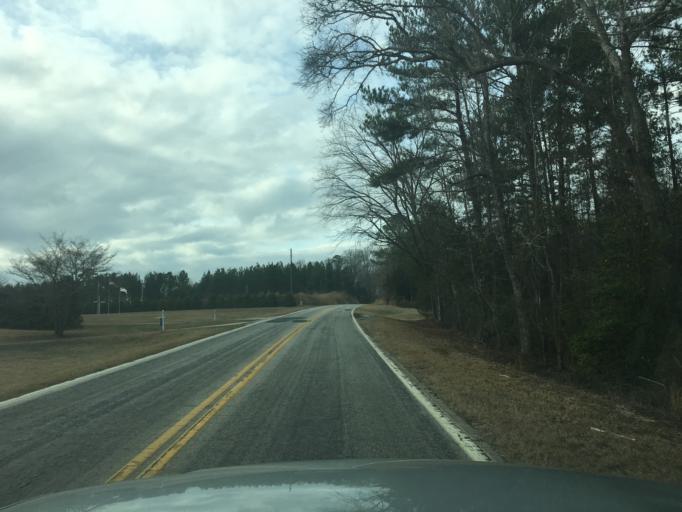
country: US
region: South Carolina
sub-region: Abbeville County
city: Due West
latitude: 34.2898
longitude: -82.4452
